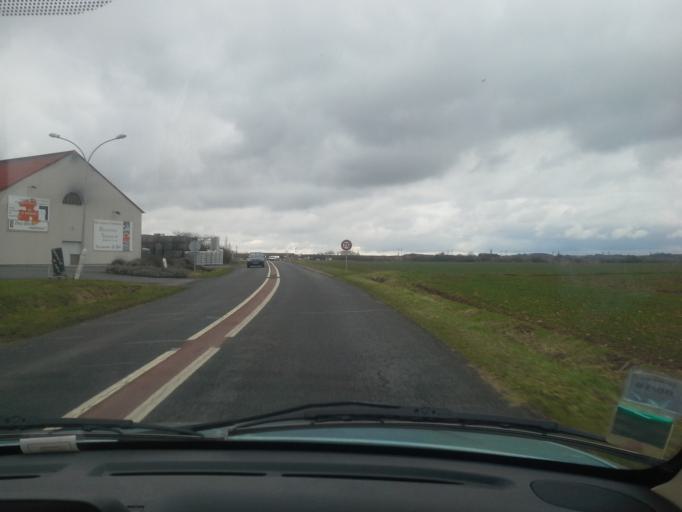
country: FR
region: Centre
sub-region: Departement du Loir-et-Cher
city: Villiers-sur-Loir
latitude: 47.7985
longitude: 1.0020
